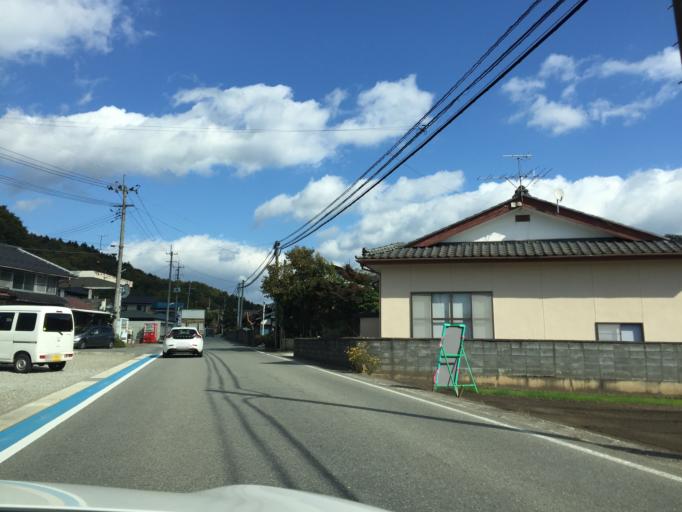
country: JP
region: Fukushima
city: Namie
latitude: 37.3290
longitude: 140.8346
